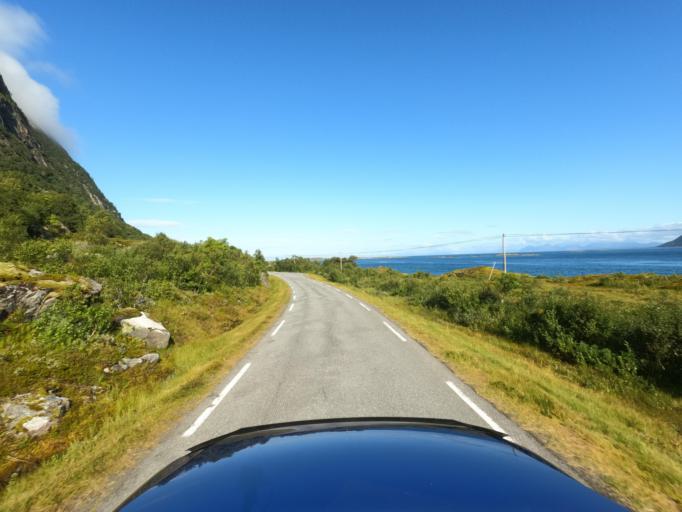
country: NO
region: Nordland
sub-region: Vagan
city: Kabelvag
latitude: 68.3085
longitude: 14.2519
